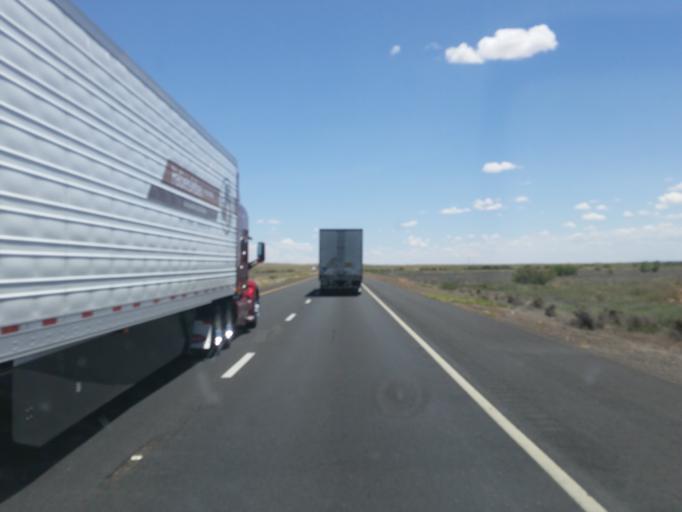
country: US
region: Arizona
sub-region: Navajo County
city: Winslow
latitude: 34.9875
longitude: -110.5620
